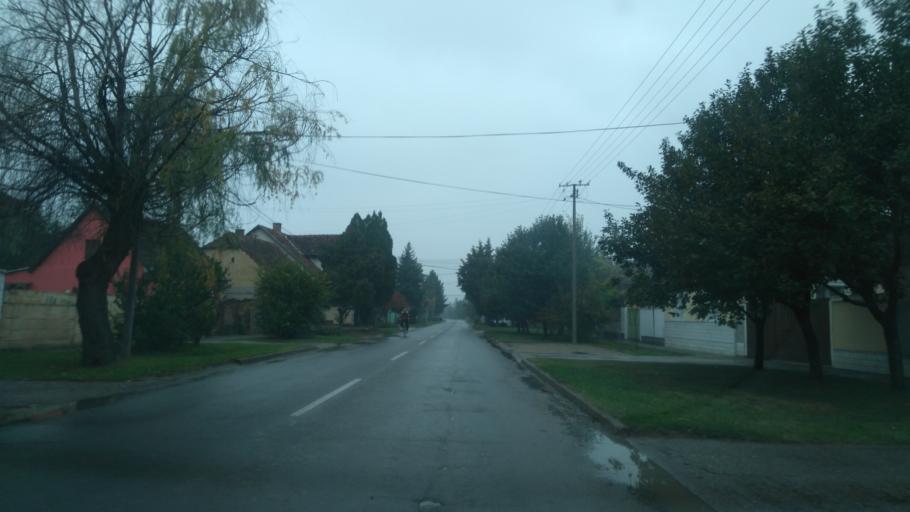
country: RS
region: Autonomna Pokrajina Vojvodina
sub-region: Juznobacki Okrug
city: Becej
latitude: 45.6241
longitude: 20.0508
